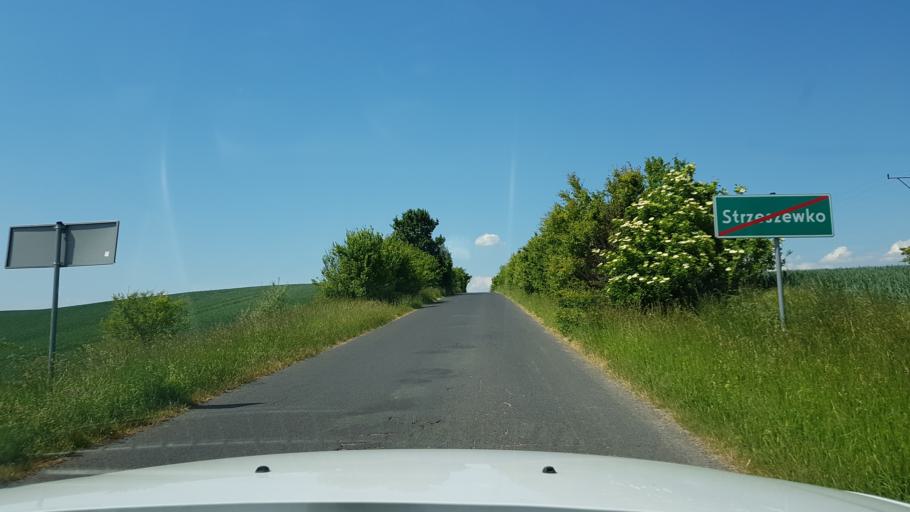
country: PL
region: West Pomeranian Voivodeship
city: Trzcinsko Zdroj
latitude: 53.0021
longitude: 14.5689
